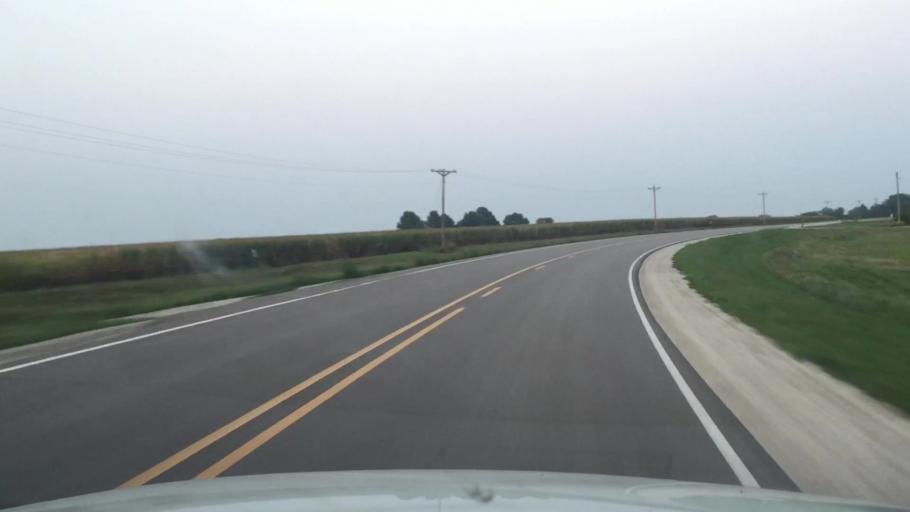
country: US
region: Iowa
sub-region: Warren County
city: Indianola
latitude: 41.1842
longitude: -93.4469
